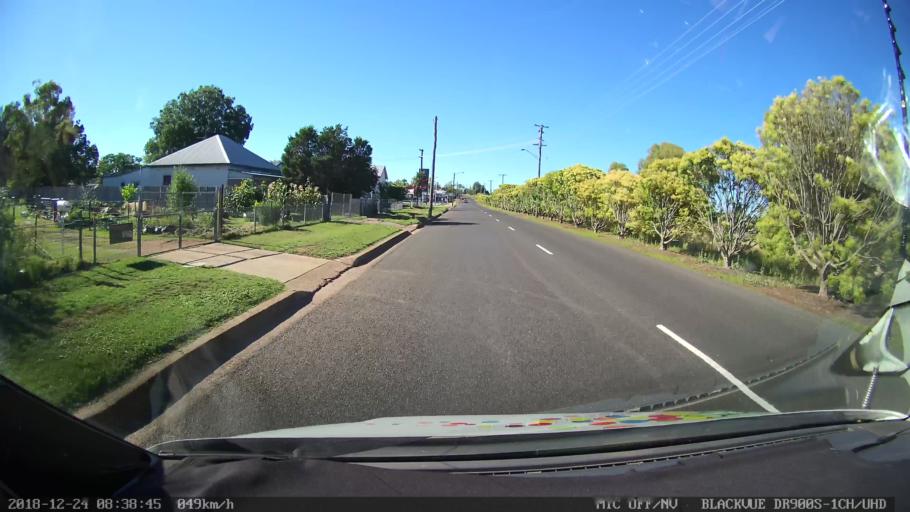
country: AU
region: New South Wales
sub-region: Liverpool Plains
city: Quirindi
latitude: -31.3432
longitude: 150.6476
